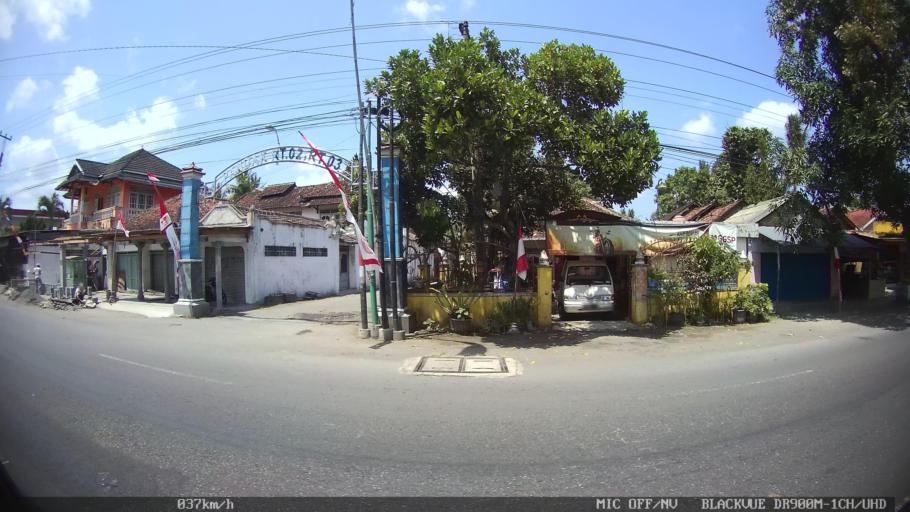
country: ID
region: Daerah Istimewa Yogyakarta
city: Pandak
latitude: -7.9110
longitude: 110.2931
